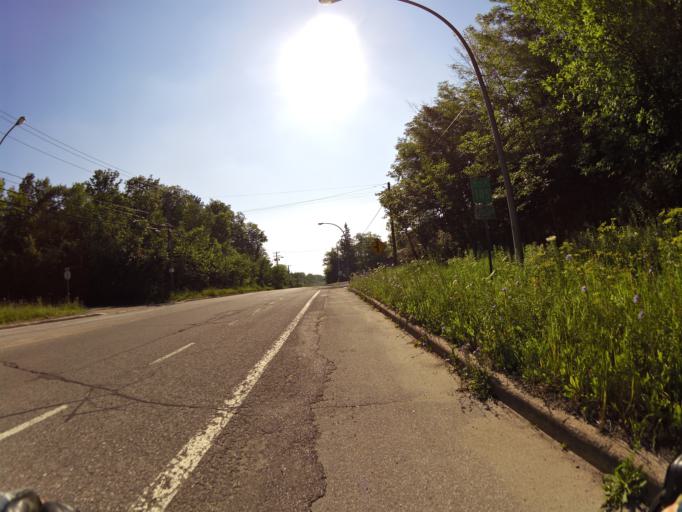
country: CA
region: Quebec
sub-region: Outaouais
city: Gatineau
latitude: 45.5255
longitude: -75.8018
